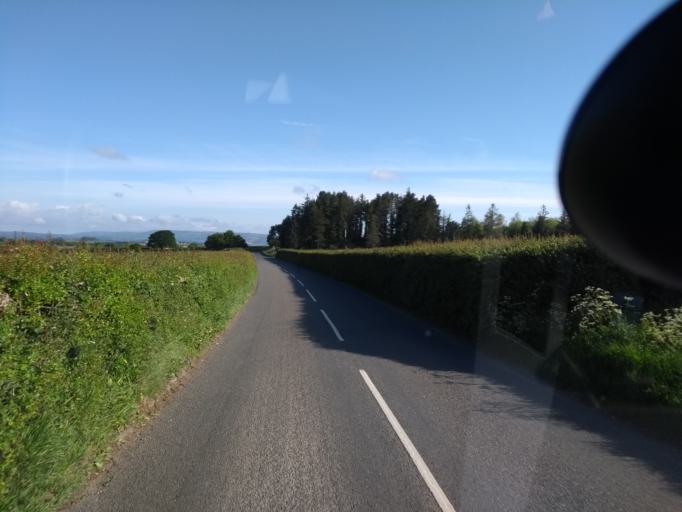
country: GB
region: England
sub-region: Somerset
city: Taunton
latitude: 50.9691
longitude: -3.1256
